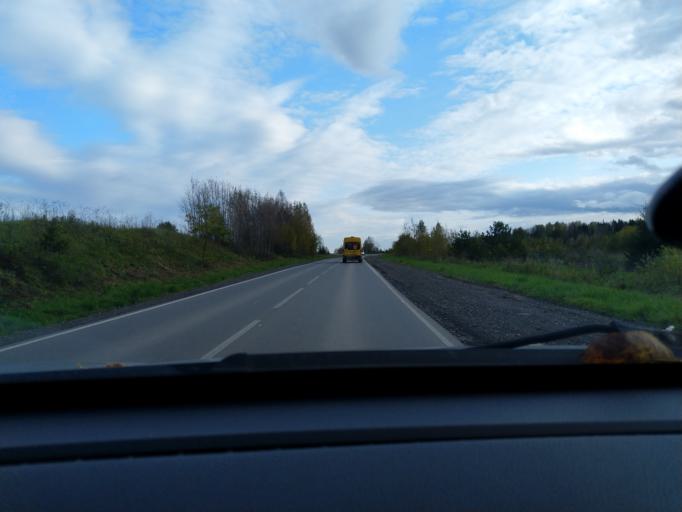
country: RU
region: Perm
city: Polazna
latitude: 58.2776
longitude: 56.4143
